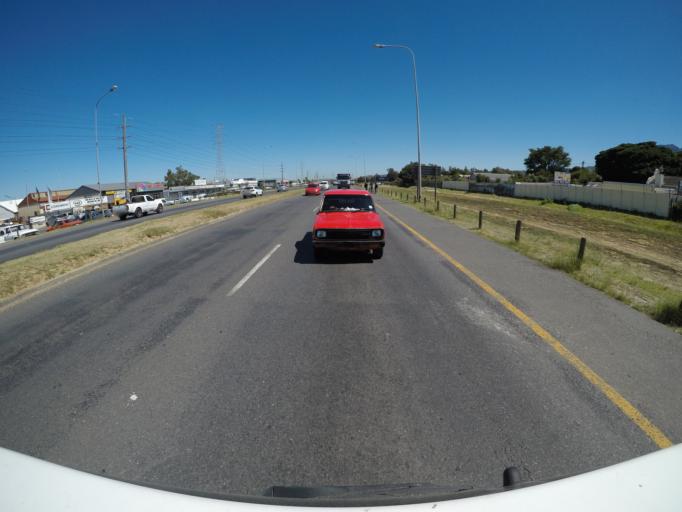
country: ZA
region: Western Cape
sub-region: Cape Winelands District Municipality
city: Stellenbosch
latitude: -34.0975
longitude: 18.8482
